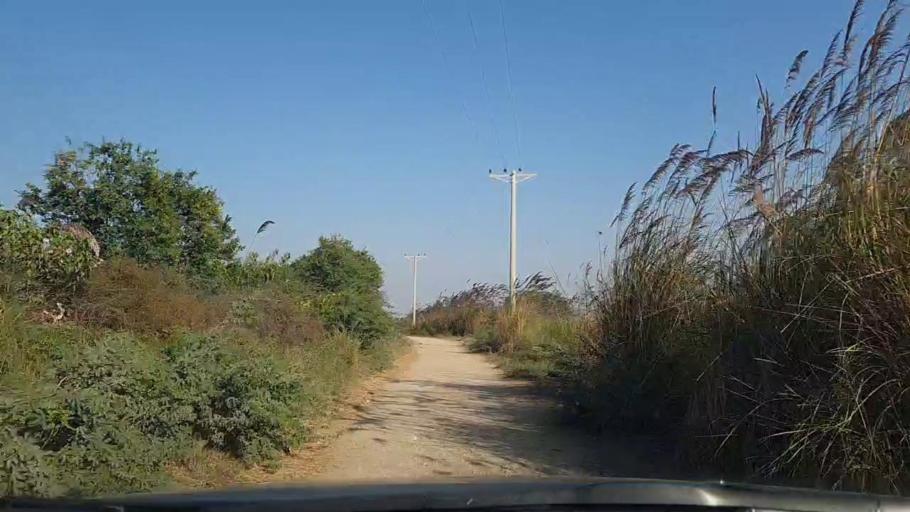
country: PK
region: Sindh
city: Mirpur Sakro
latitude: 24.5409
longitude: 67.6421
